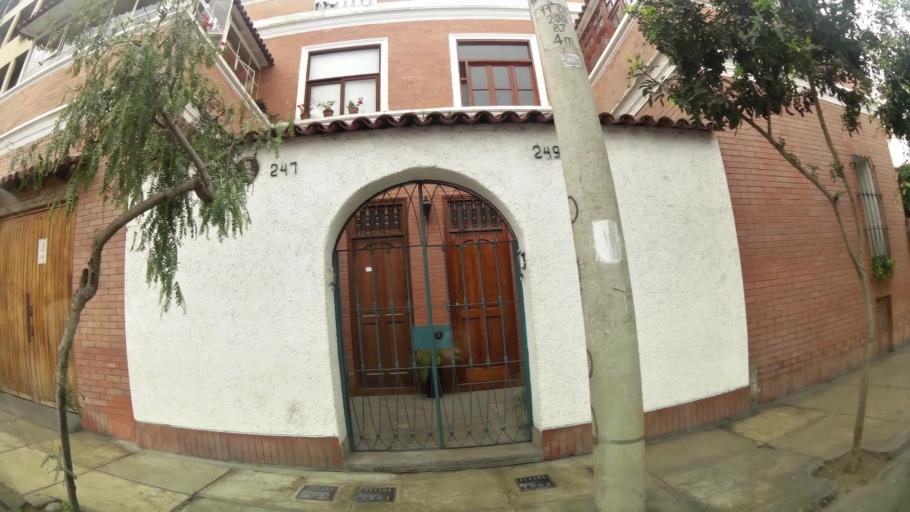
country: PE
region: Lima
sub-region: Lima
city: San Isidro
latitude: -12.1208
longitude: -77.0390
